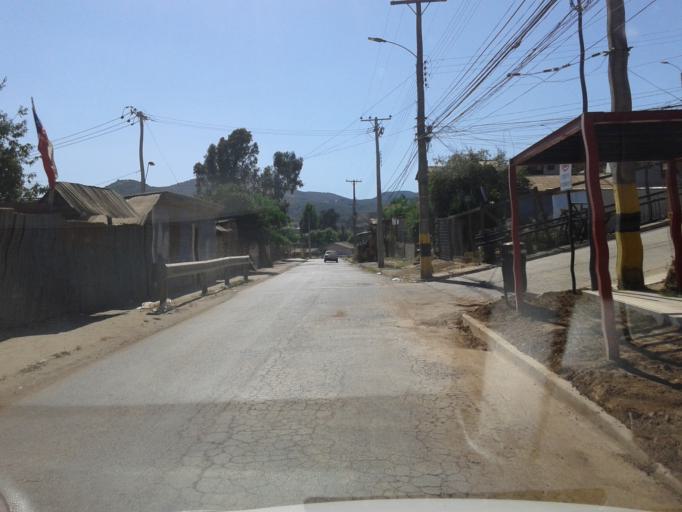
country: CL
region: Valparaiso
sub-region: Provincia de Quillota
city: Quillota
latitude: -32.8758
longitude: -71.2552
